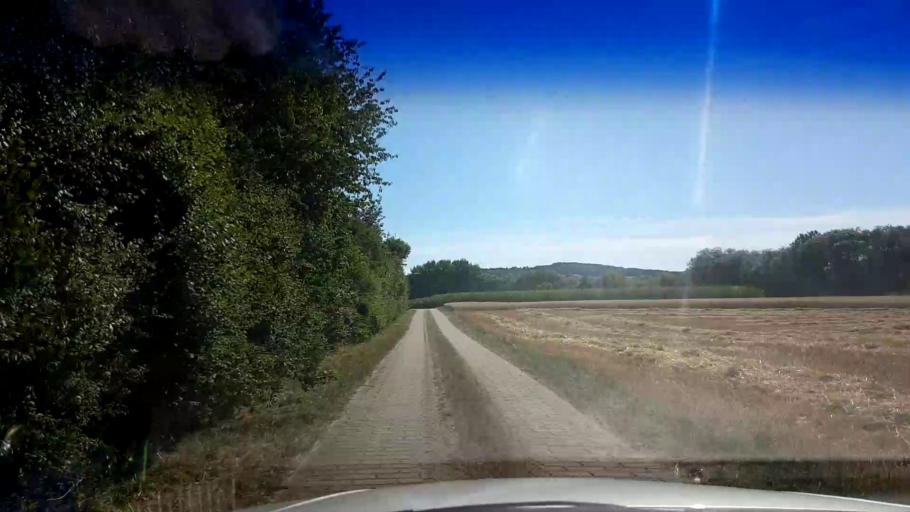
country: DE
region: Bavaria
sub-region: Upper Franconia
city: Viereth-Trunstadt
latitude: 49.9373
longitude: 10.7642
